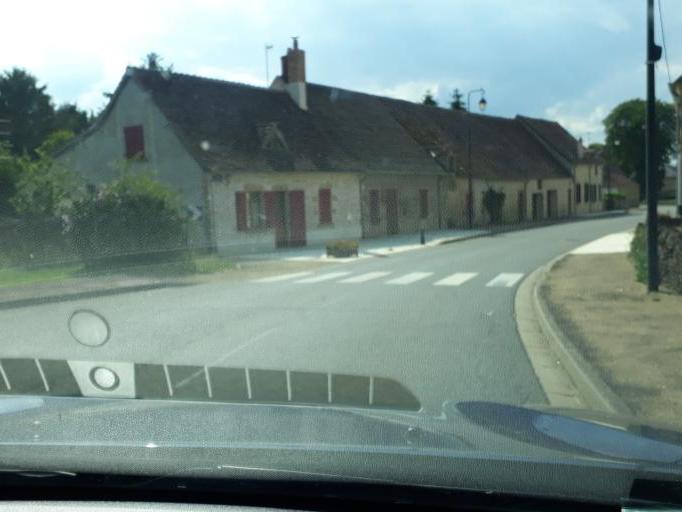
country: FR
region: Centre
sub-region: Departement du Cher
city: Nerondes
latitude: 47.0483
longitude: 2.8730
